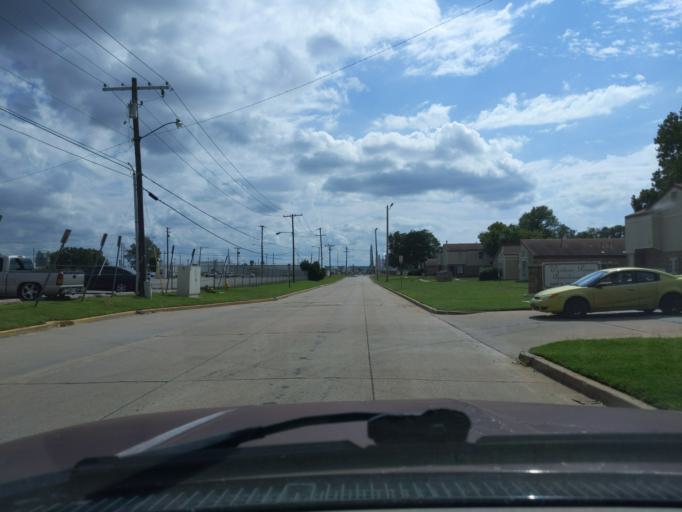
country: US
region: Oklahoma
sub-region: Tulsa County
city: Tulsa
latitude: 36.1283
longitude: -95.9995
